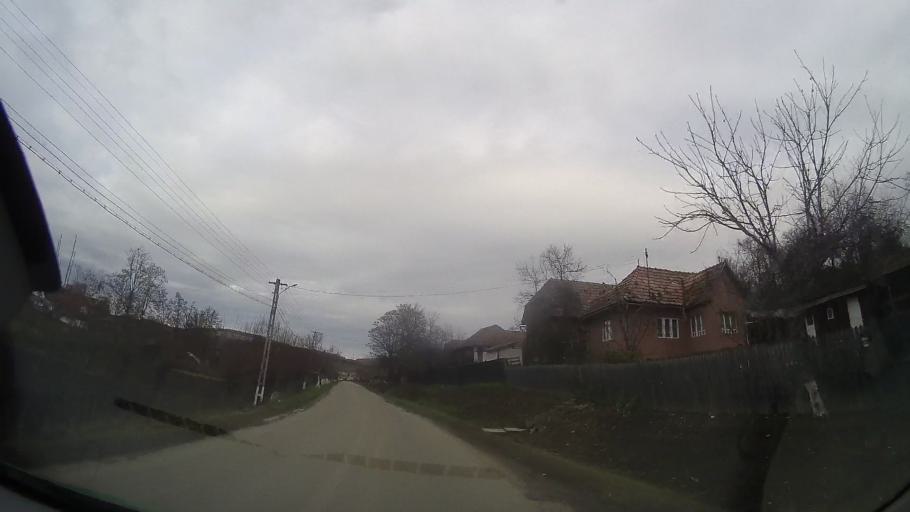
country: RO
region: Mures
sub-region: Comuna Faragau
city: Faragau
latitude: 46.7598
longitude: 24.5172
